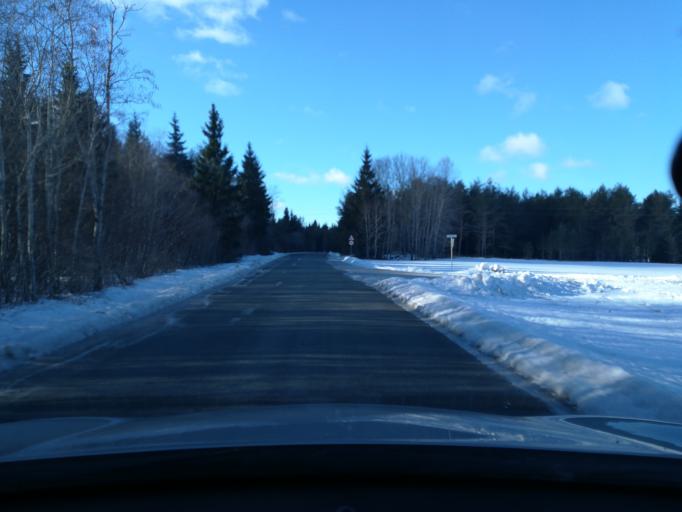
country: EE
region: Harju
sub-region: Kiili vald
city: Kiili
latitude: 59.2641
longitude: 24.8123
